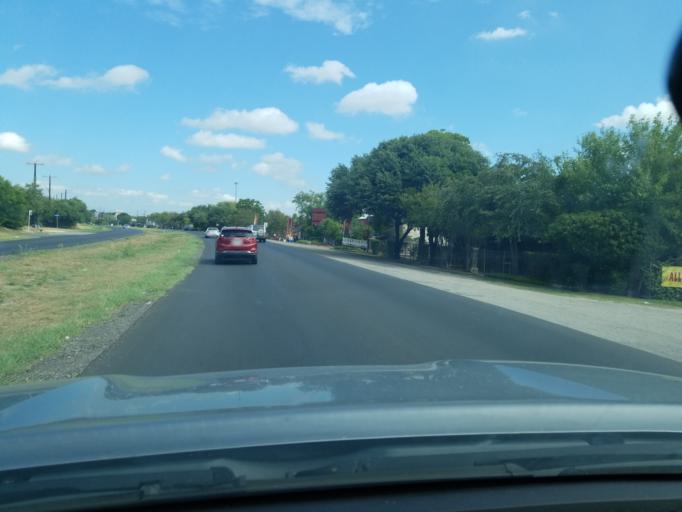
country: US
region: Texas
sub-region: Bexar County
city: Terrell Hills
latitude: 29.4874
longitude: -98.4299
